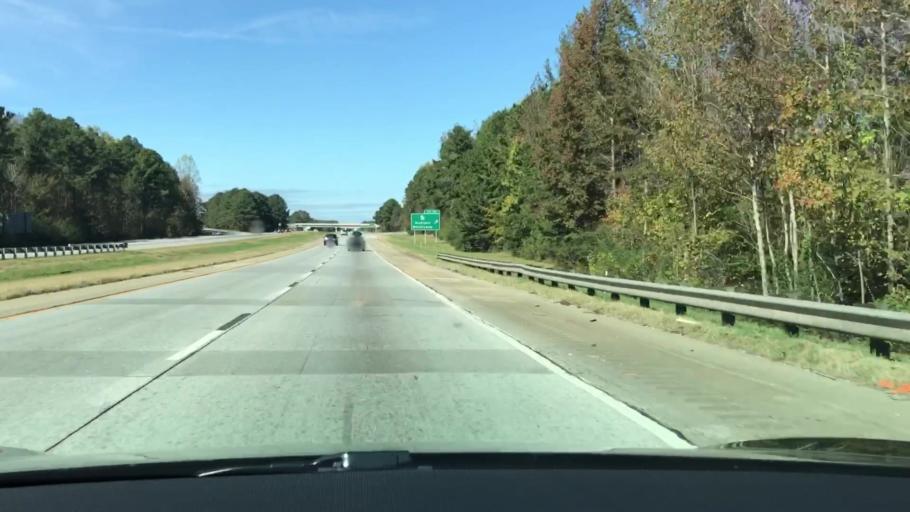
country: US
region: Georgia
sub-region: Morgan County
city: Madison
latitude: 33.5583
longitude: -83.4925
